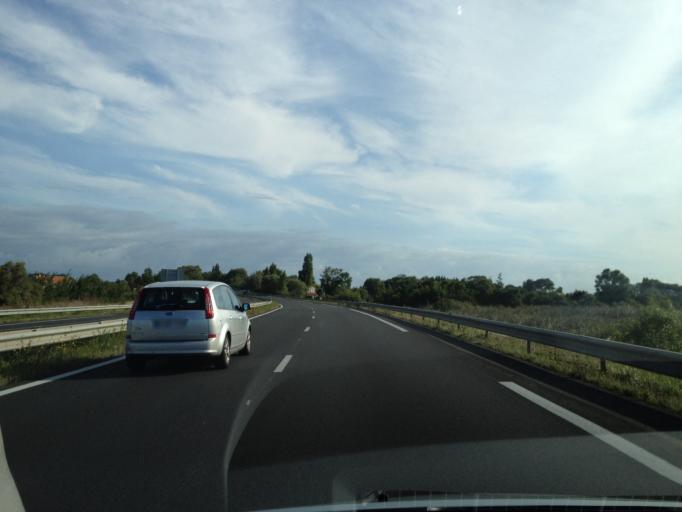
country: FR
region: Poitou-Charentes
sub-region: Departement de la Charente-Maritime
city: Yves
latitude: 46.0374
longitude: -1.0482
